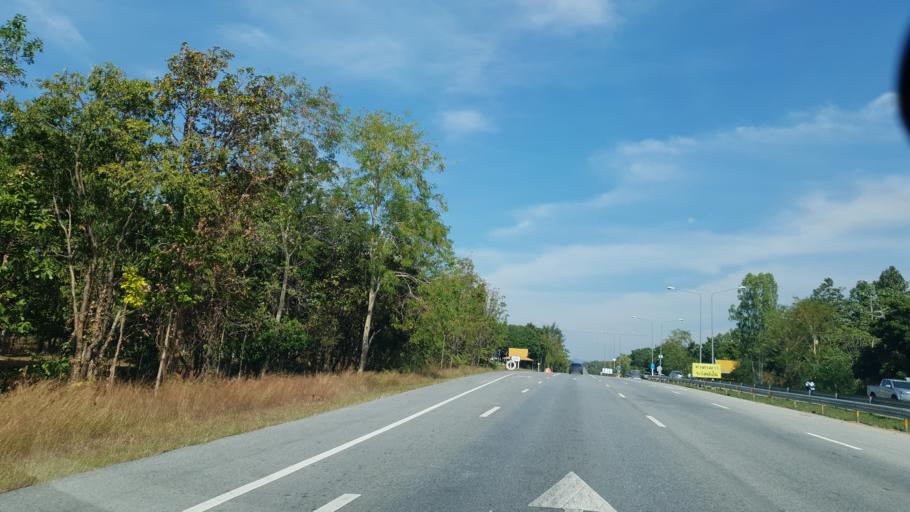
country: TH
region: Uttaradit
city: Thong Saen Khan
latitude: 17.4324
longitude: 100.2280
